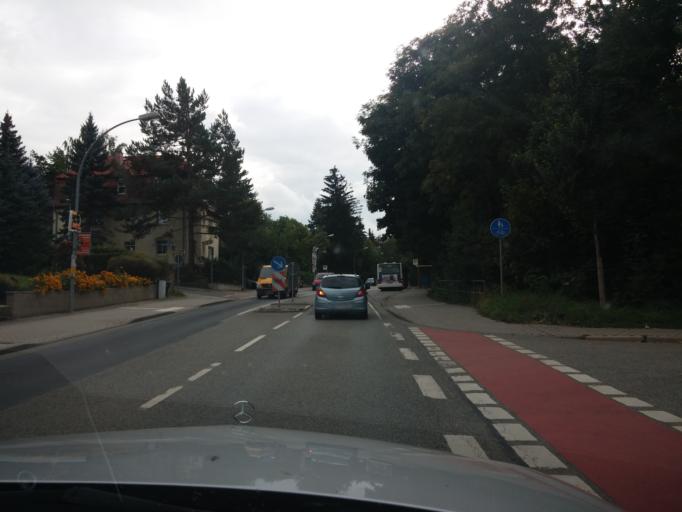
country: DE
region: Thuringia
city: Weimar
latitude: 50.9689
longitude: 11.3241
